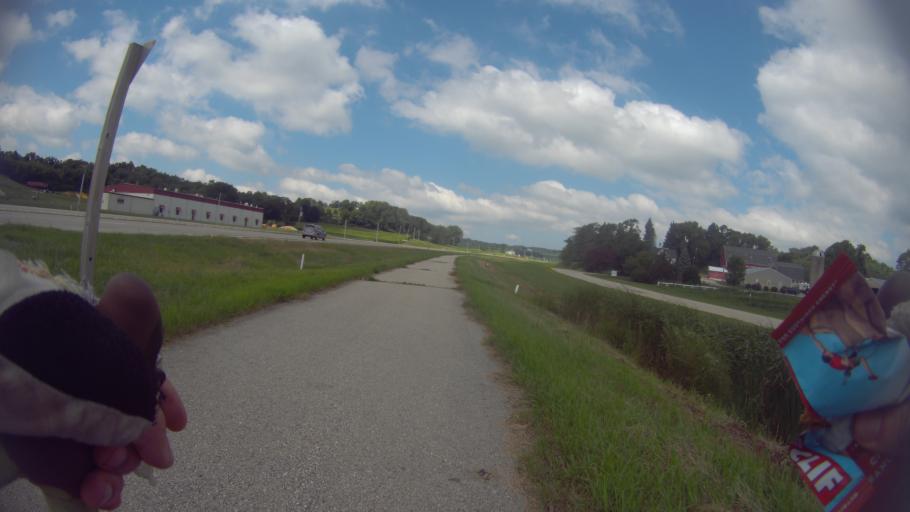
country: US
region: Wisconsin
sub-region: Dane County
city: Cross Plains
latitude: 43.1929
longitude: -89.5727
